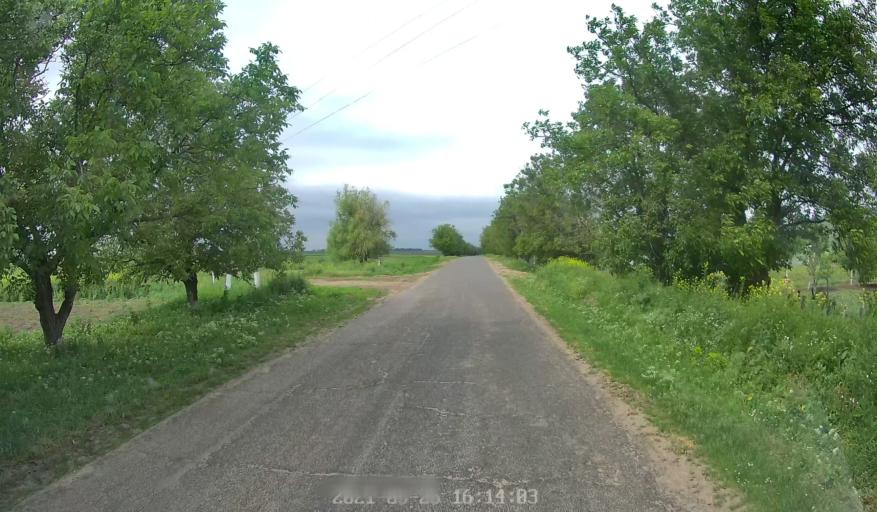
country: MD
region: Hincesti
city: Dancu
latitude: 46.7064
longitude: 28.3401
